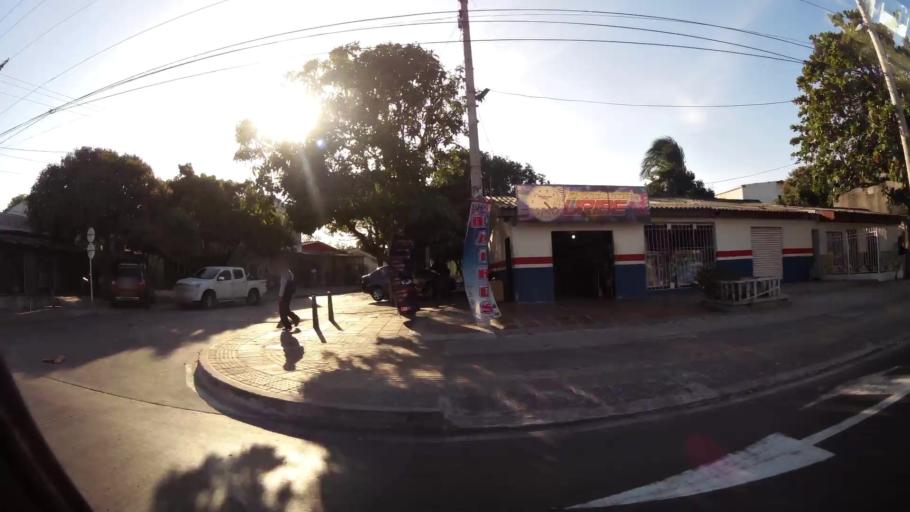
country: CO
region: Atlantico
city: Barranquilla
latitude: 10.9434
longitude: -74.7997
